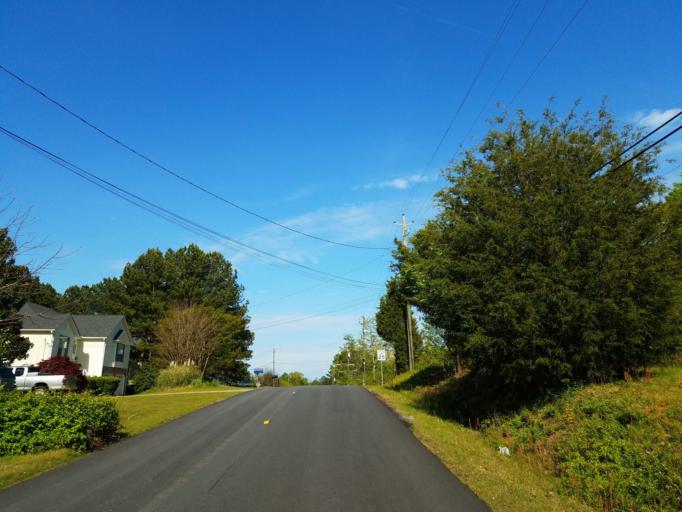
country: US
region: Georgia
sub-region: Douglas County
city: Lithia Springs
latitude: 33.7067
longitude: -84.6546
